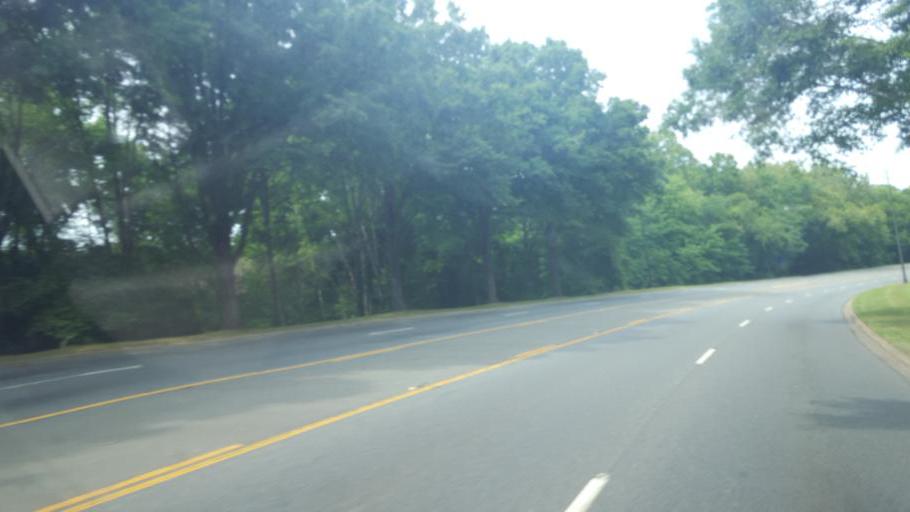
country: US
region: South Carolina
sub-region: York County
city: Rock Hill
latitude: 34.9335
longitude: -81.0155
